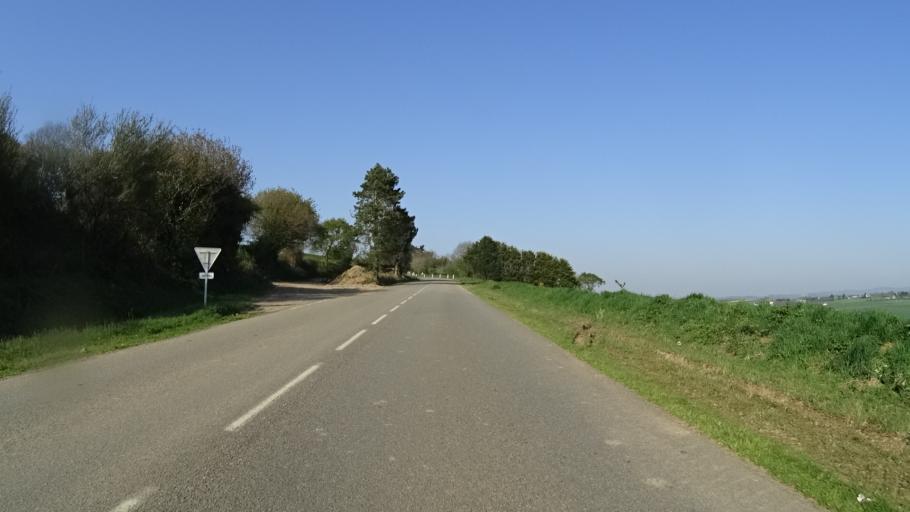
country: FR
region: Brittany
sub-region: Departement du Finistere
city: Irvillac
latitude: 48.3625
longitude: -4.2310
